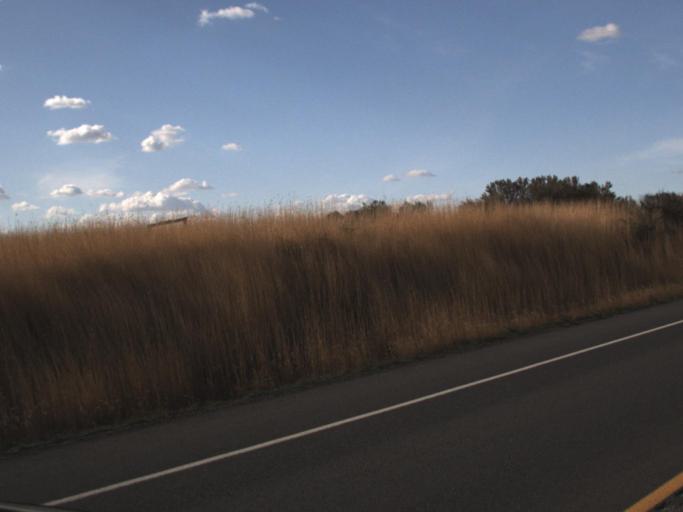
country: US
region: Oregon
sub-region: Umatilla County
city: Umatilla
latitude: 45.9524
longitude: -119.4041
